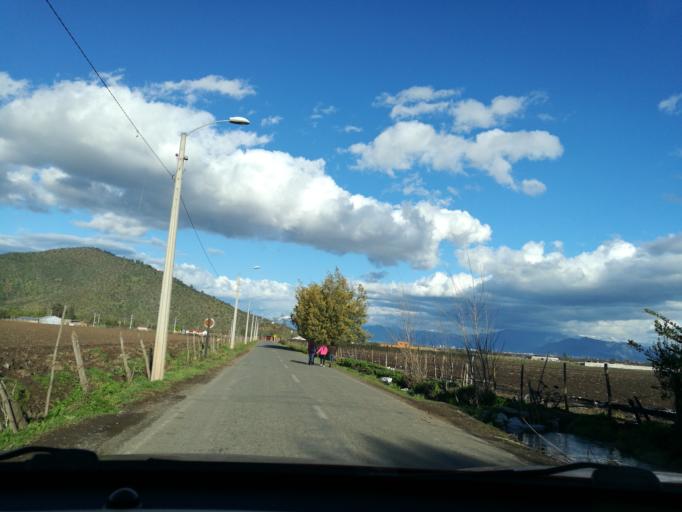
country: CL
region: O'Higgins
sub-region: Provincia de Cachapoal
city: Graneros
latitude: -34.0927
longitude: -70.8266
